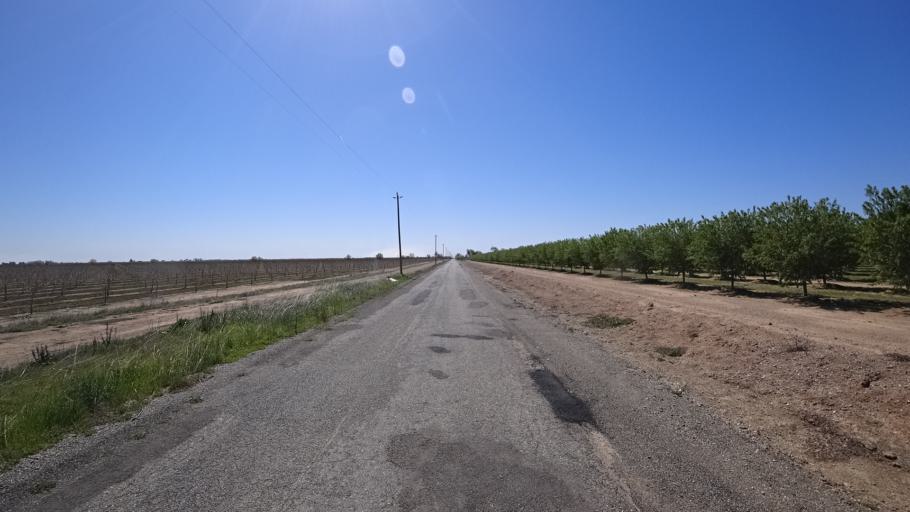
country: US
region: California
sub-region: Glenn County
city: Orland
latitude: 39.6381
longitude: -122.2346
